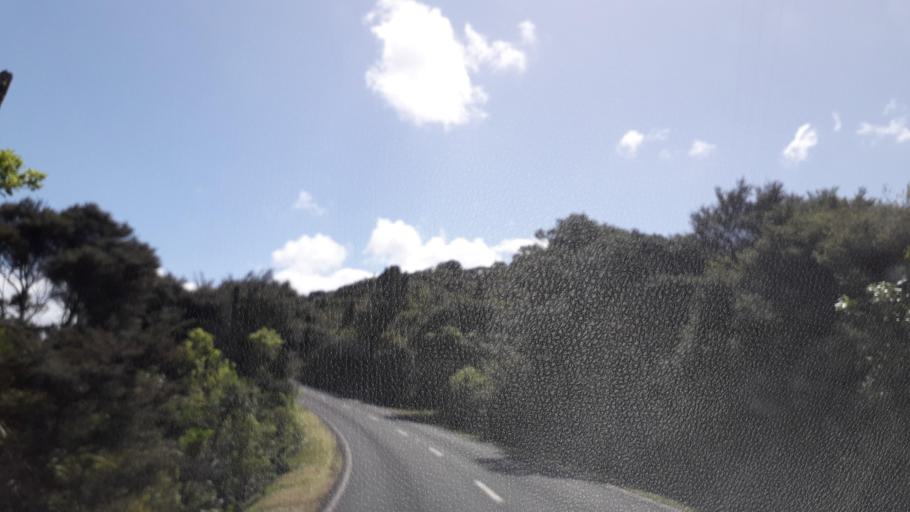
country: NZ
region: Northland
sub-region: Far North District
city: Paihia
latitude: -35.2481
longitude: 174.2580
